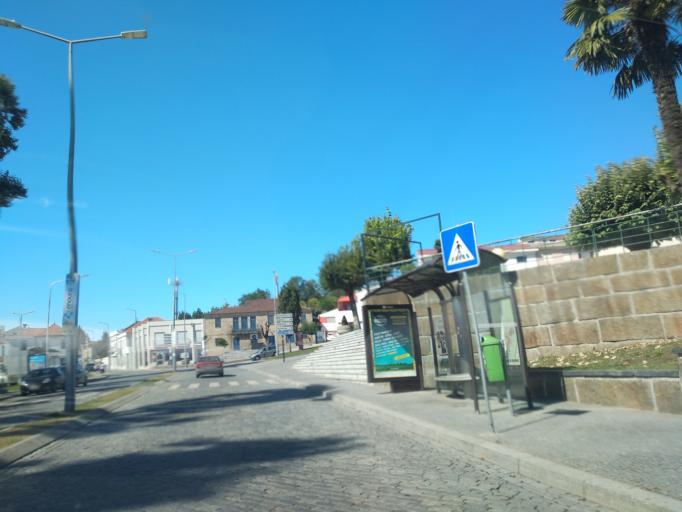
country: PT
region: Porto
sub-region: Pacos de Ferreira
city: Freamunde
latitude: 41.2889
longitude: -8.3404
